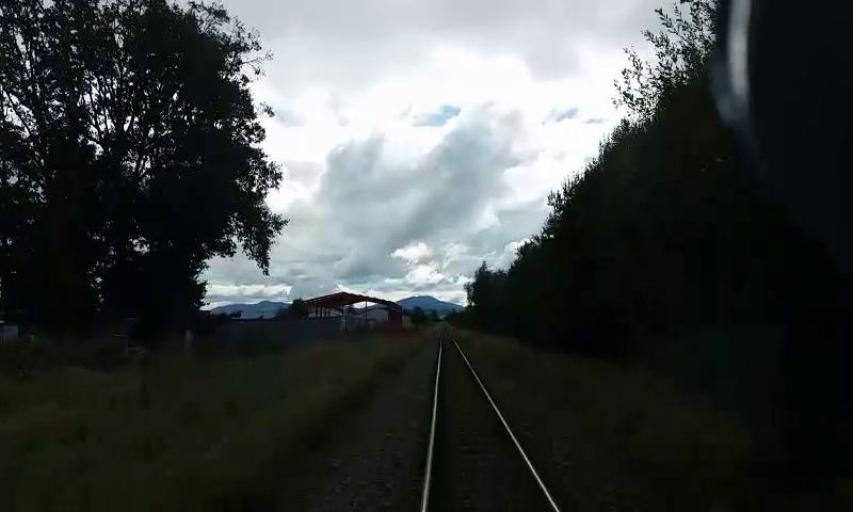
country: NZ
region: Canterbury
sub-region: Waimakariri District
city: Woodend
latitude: -43.3150
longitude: 172.6012
